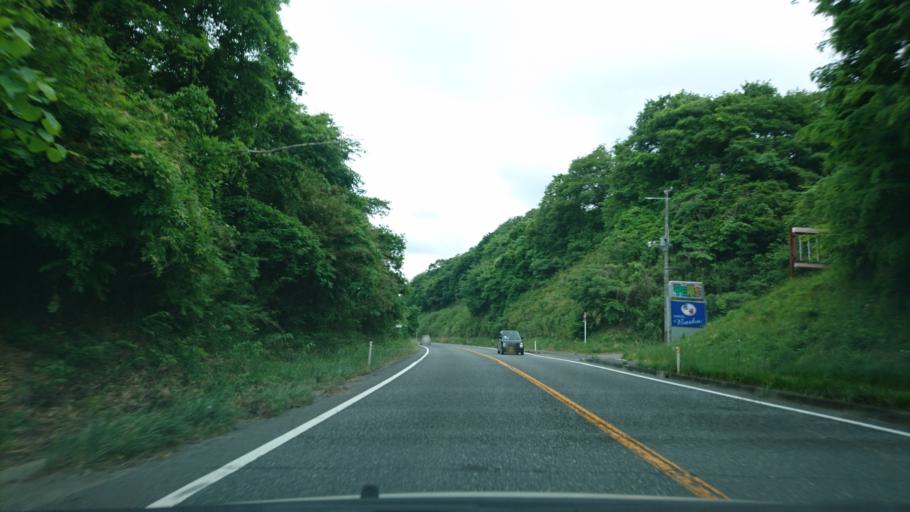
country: JP
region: Iwate
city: Ichinoseki
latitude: 38.8964
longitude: 141.1150
